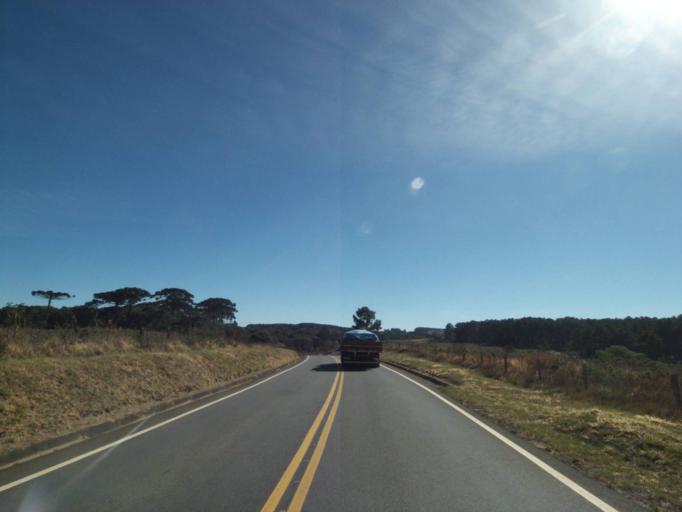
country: BR
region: Parana
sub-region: Castro
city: Castro
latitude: -24.7308
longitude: -50.1822
